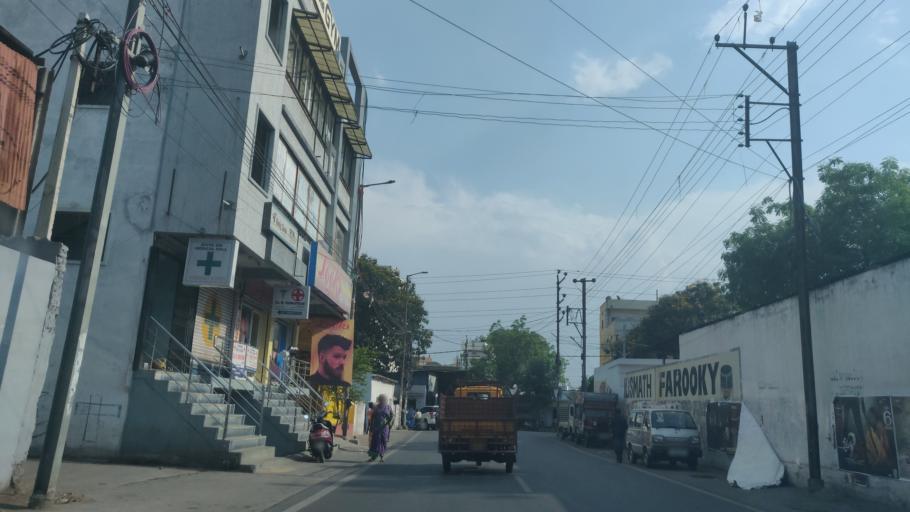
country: IN
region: Telangana
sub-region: Rangareddi
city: Gaddi Annaram
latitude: 17.3881
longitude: 78.5112
